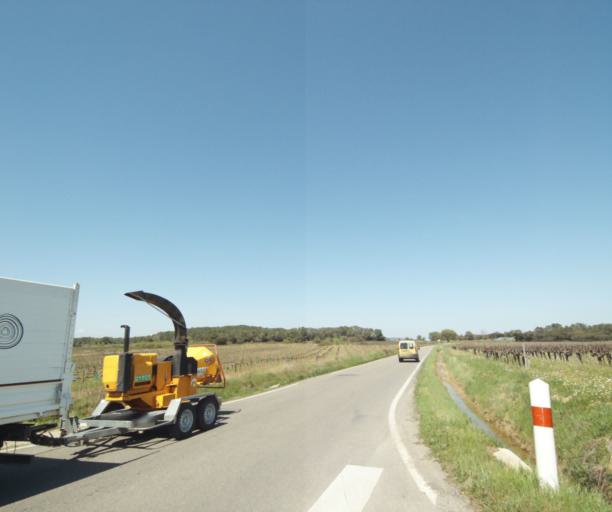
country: FR
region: Languedoc-Roussillon
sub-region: Departement de l'Herault
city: Beaulieu
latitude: 43.7326
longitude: 4.0097
